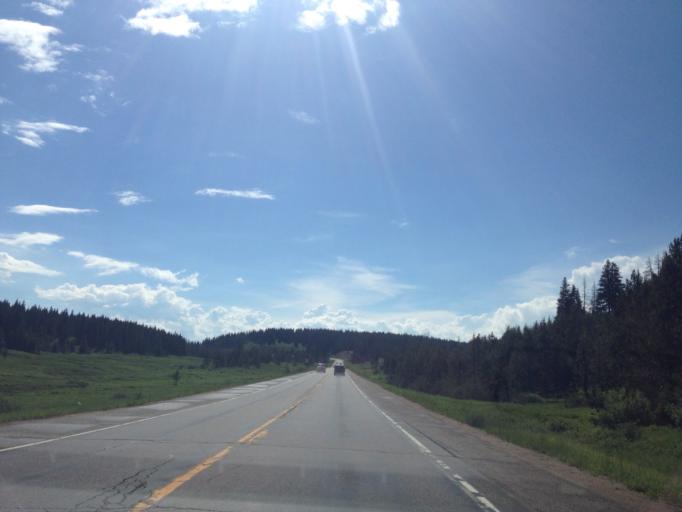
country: US
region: Colorado
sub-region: Routt County
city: Steamboat Springs
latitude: 40.3891
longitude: -106.6629
